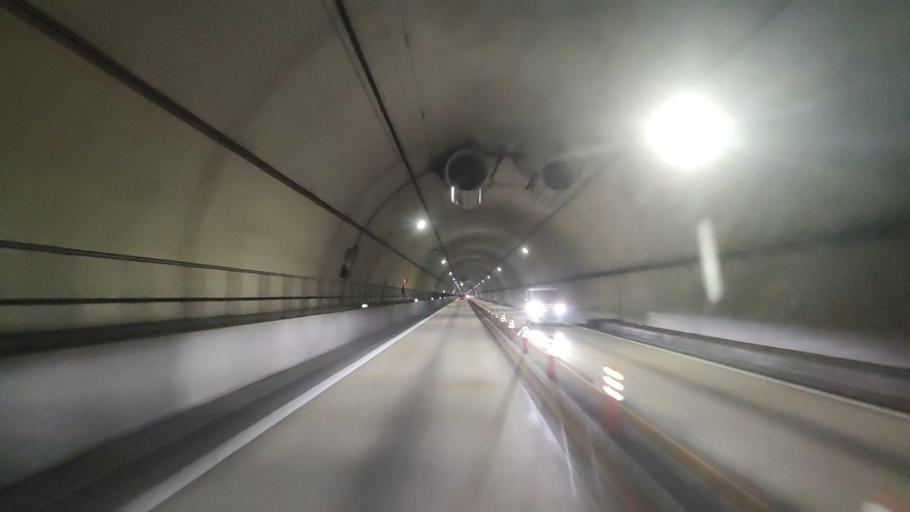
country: JP
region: Wakayama
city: Tanabe
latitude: 33.5682
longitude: 135.4890
